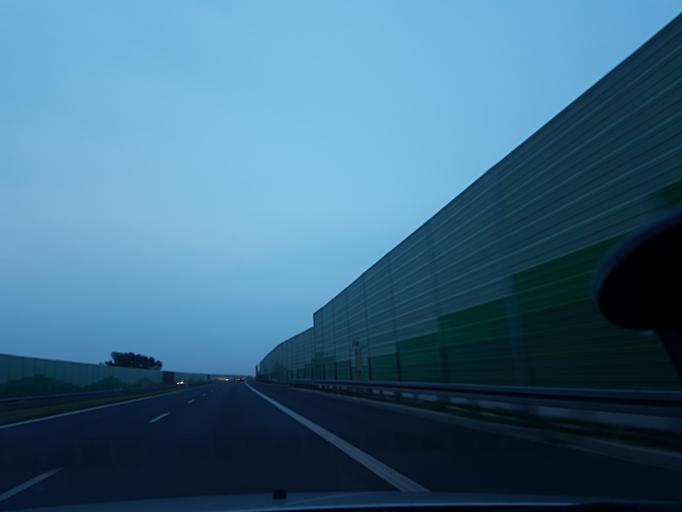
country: PL
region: Lodz Voivodeship
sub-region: Powiat leczycki
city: Piatek
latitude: 52.1178
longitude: 19.5025
